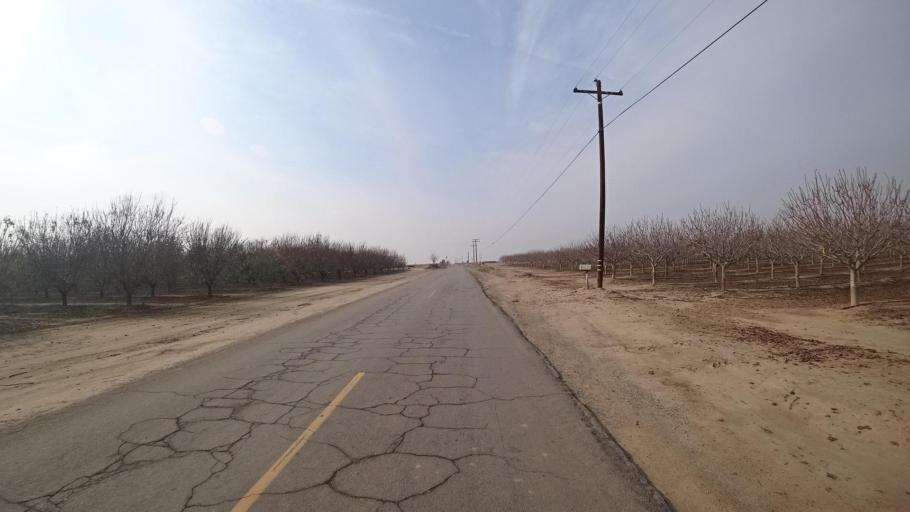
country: US
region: California
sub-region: Kern County
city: Weedpatch
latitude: 35.1366
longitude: -118.9658
